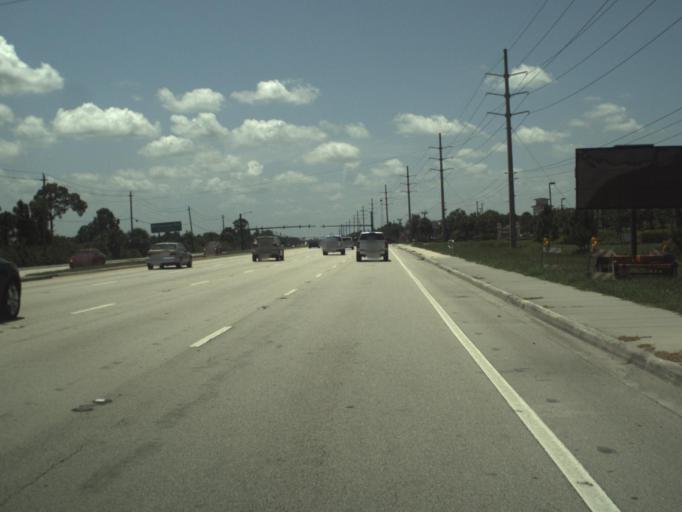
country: US
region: Florida
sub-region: Martin County
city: North River Shores
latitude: 27.2618
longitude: -80.2831
